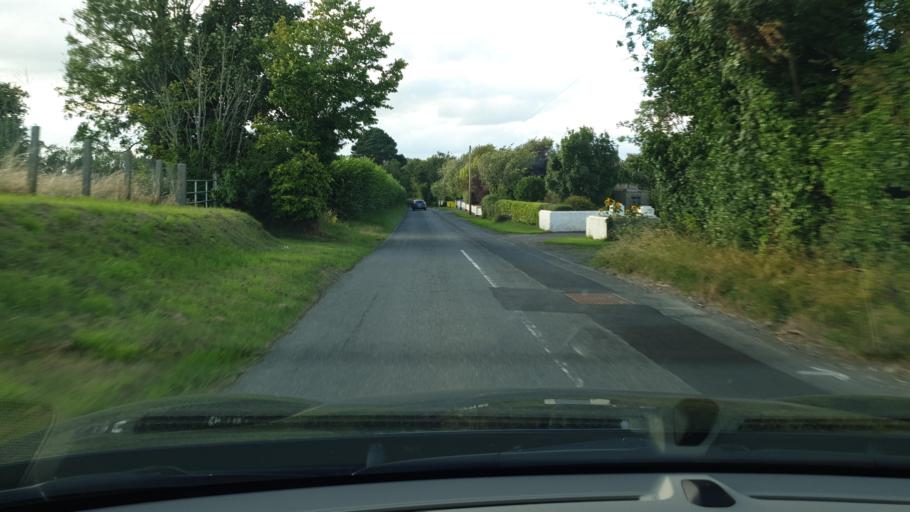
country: IE
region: Leinster
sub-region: Lu
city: Drogheda
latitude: 53.6780
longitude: -6.3280
